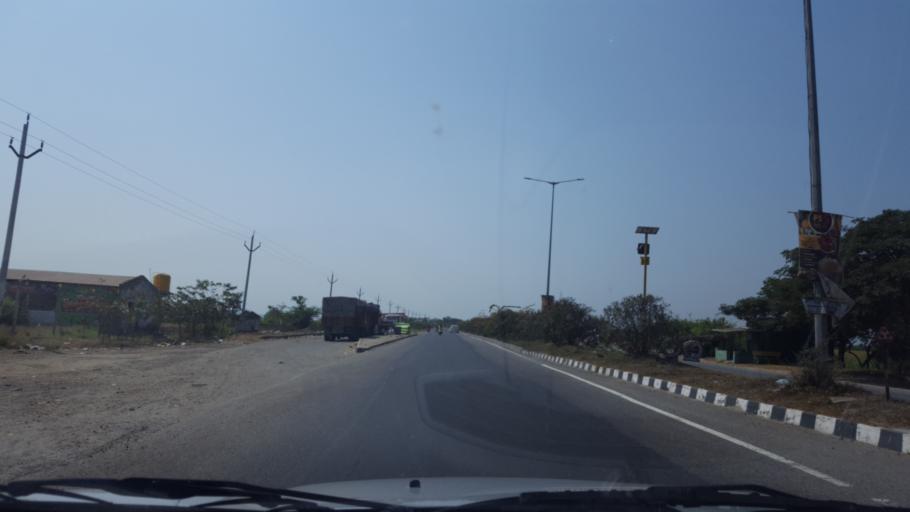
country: IN
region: Andhra Pradesh
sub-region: Guntur
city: Chilakalurupet
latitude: 16.0598
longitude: 80.1483
